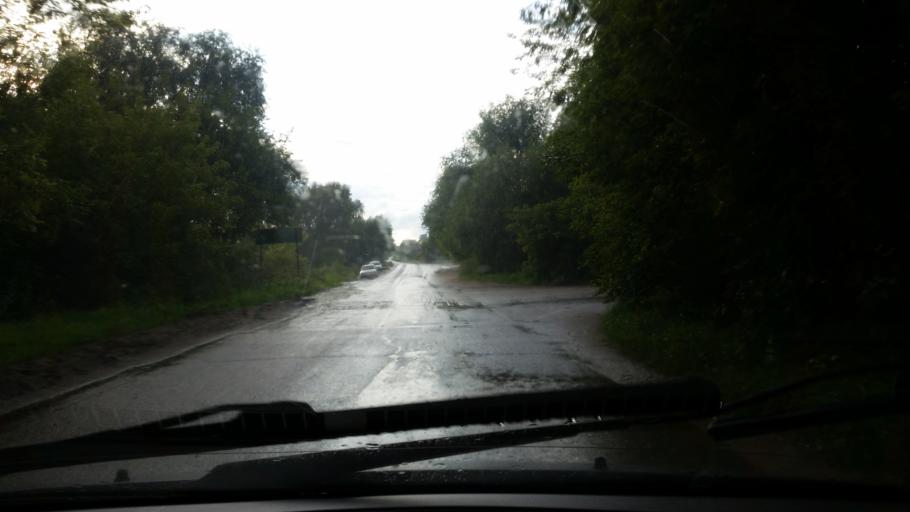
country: RU
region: Moskovskaya
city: Bol'shoye Gryzlovo
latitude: 54.8767
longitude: 37.8210
